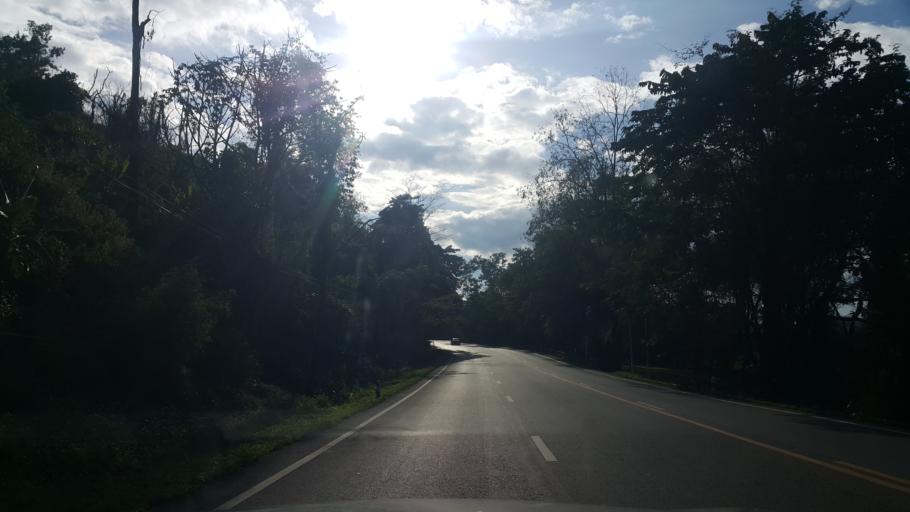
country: TH
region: Phayao
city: Phayao
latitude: 19.0602
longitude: 99.7981
